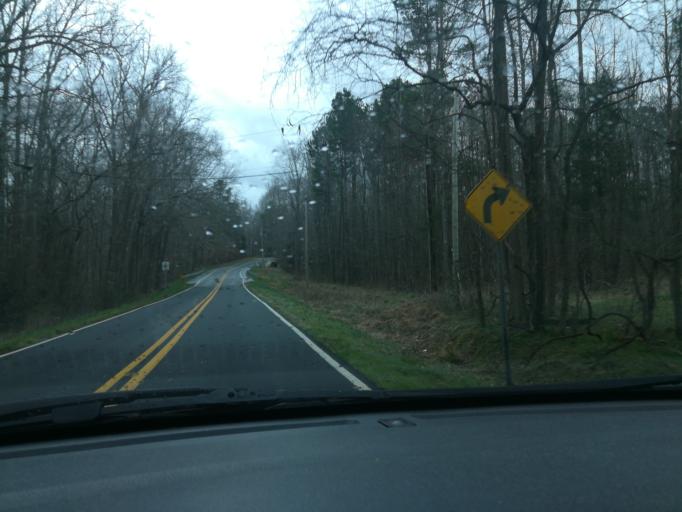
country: US
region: North Carolina
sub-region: Orange County
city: Hillsborough
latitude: 36.0281
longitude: -79.0608
